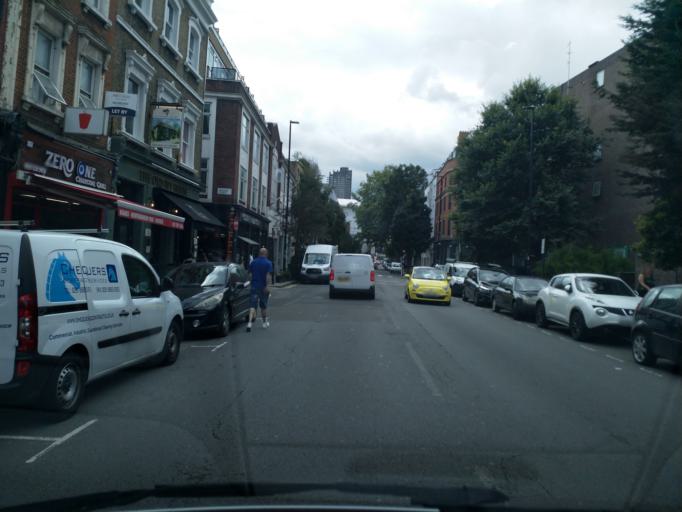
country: GB
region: England
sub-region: Greater London
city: Barbican
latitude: 51.5260
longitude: -0.0999
